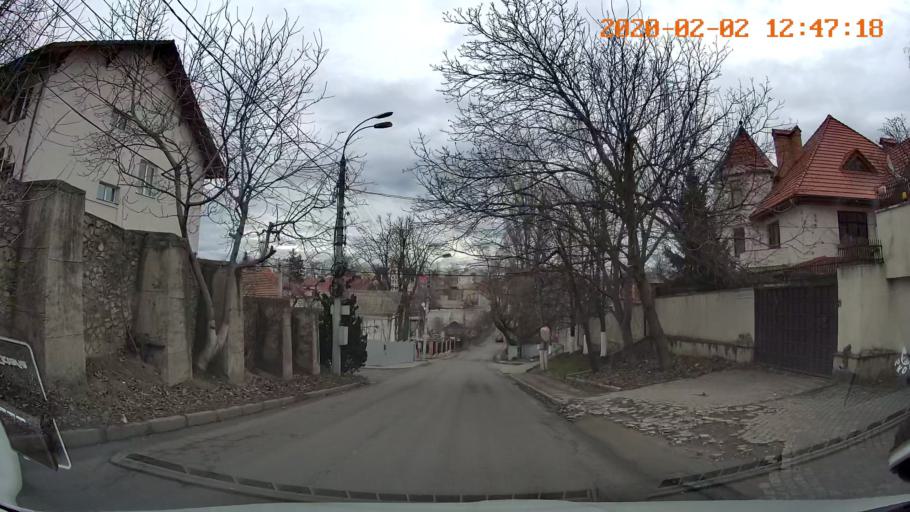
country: MD
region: Chisinau
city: Chisinau
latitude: 47.0123
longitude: 28.8239
